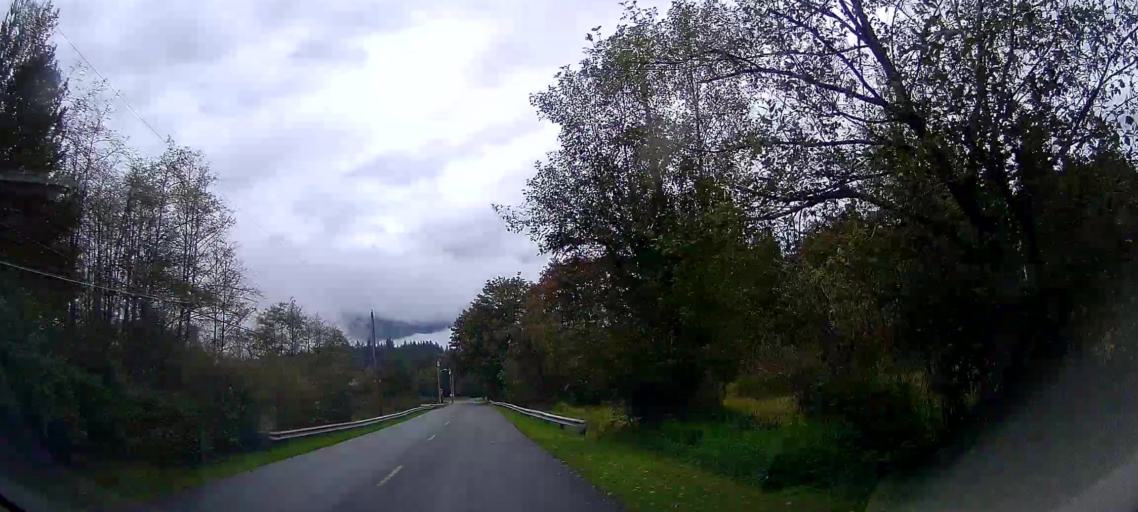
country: US
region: Washington
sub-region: Skagit County
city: Sedro-Woolley
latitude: 48.5266
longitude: -121.9901
